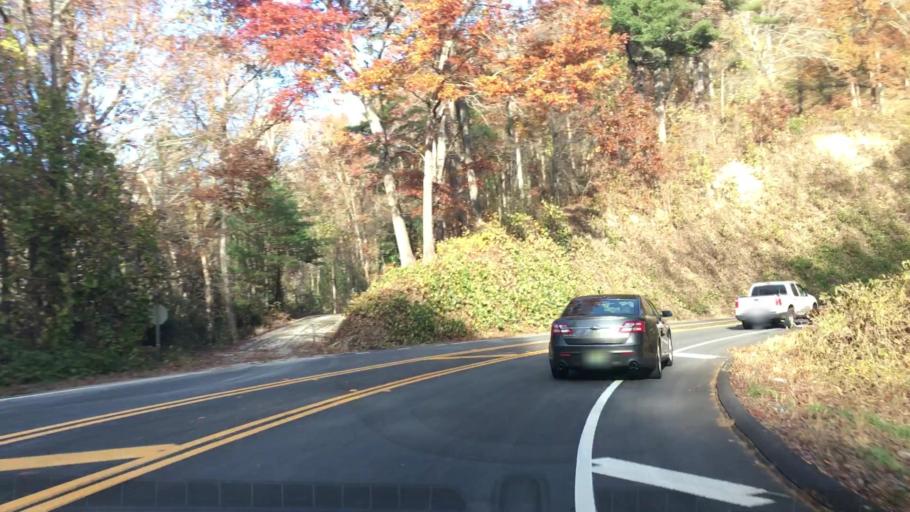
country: US
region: Georgia
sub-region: Rabun County
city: Mountain City
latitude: 34.9966
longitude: -83.3542
